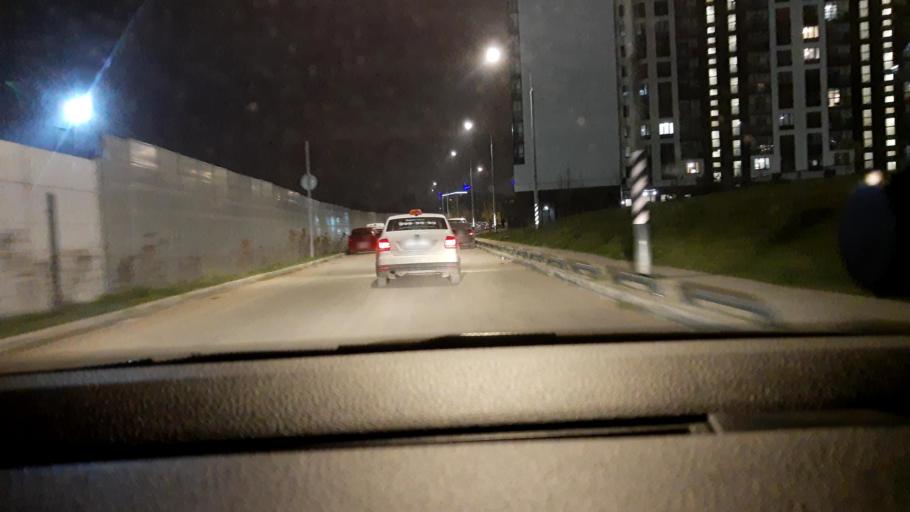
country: RU
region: Moskovskaya
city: Mosrentgen
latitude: 55.5949
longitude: 37.4621
